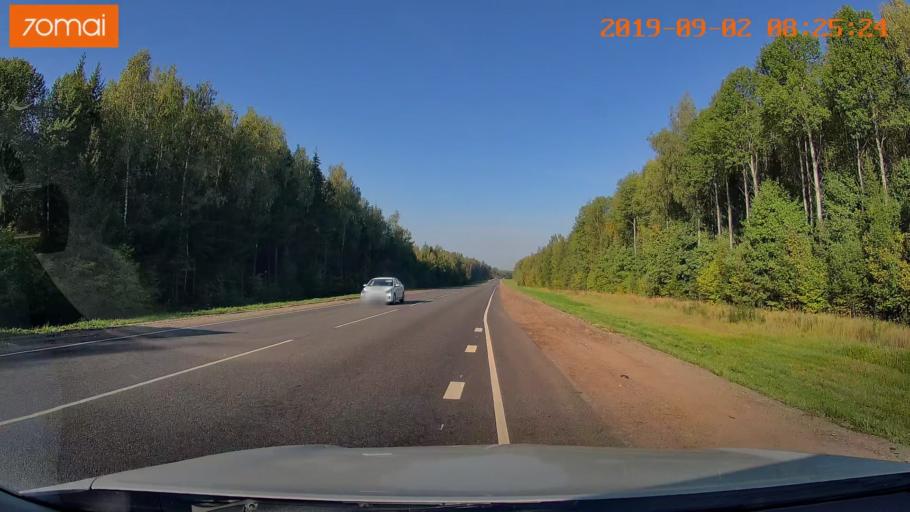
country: RU
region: Kaluga
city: Maloyaroslavets
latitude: 54.9794
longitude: 36.4634
